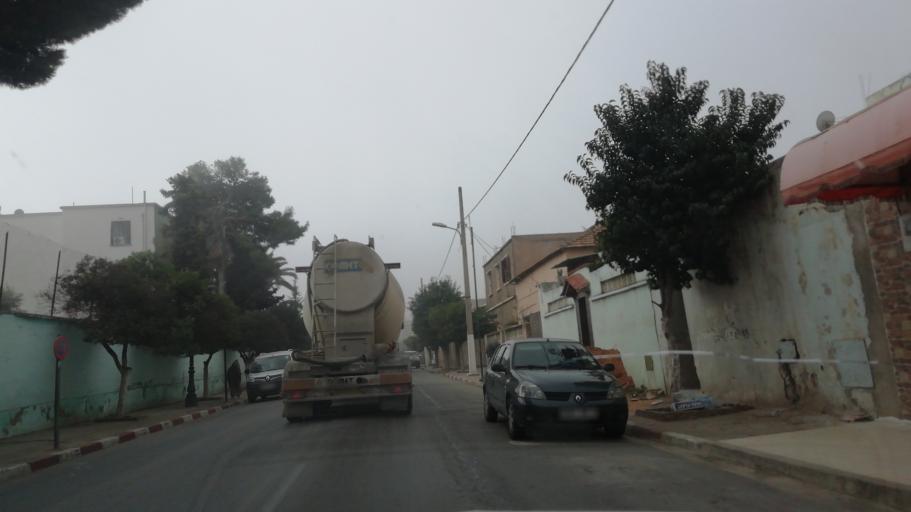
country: DZ
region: Mascara
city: Mascara
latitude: 35.5160
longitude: 0.3021
